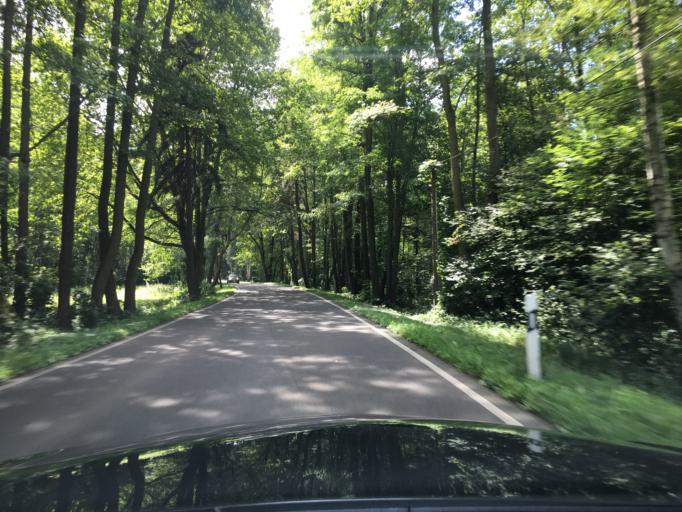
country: DE
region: Brandenburg
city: Burg
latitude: 51.8290
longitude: 14.1037
